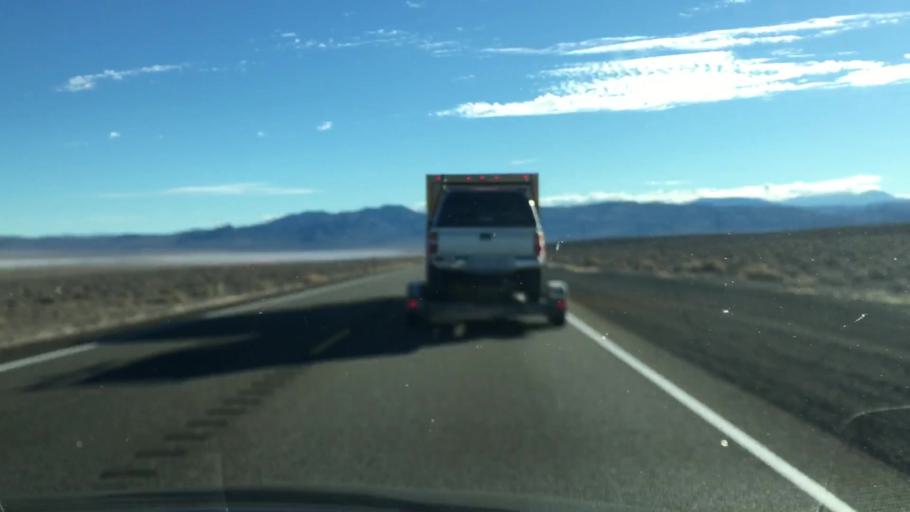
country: US
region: Nevada
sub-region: Mineral County
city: Hawthorne
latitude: 38.3346
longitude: -118.1031
